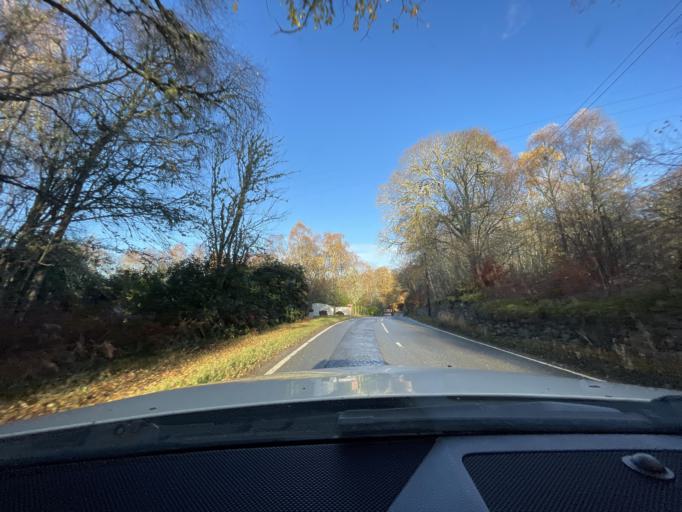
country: GB
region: Scotland
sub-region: Highland
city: Inverness
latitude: 57.4411
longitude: -4.2631
